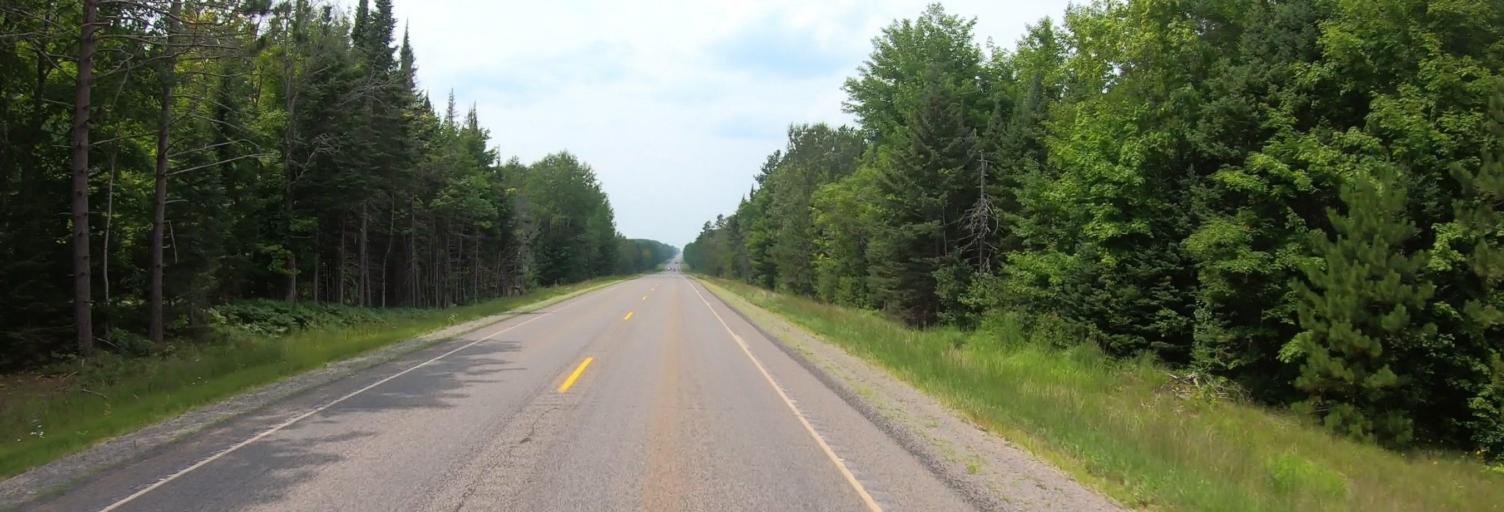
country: US
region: Michigan
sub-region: Alger County
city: Munising
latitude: 46.3329
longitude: -86.7543
